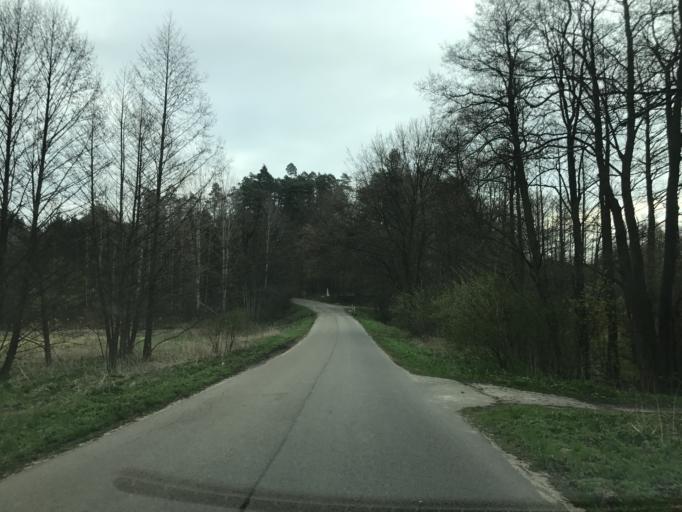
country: PL
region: Warmian-Masurian Voivodeship
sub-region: Powiat ostrodzki
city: Gierzwald
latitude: 53.6369
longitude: 20.0833
